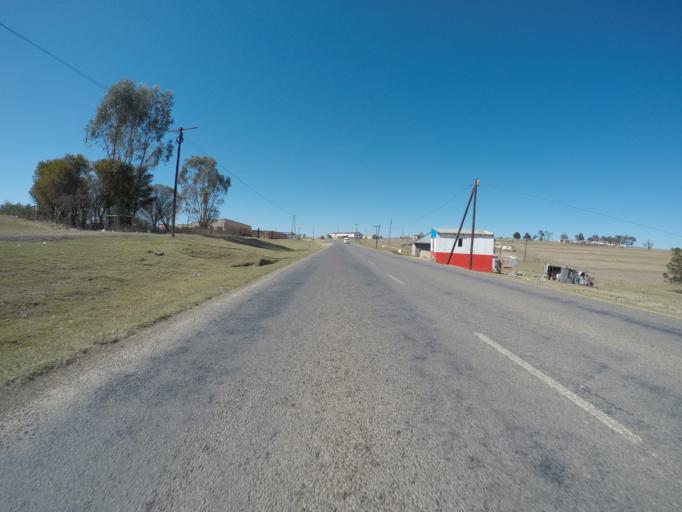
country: ZA
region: Eastern Cape
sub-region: OR Tambo District Municipality
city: Mthatha
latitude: -31.8735
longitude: 28.7533
